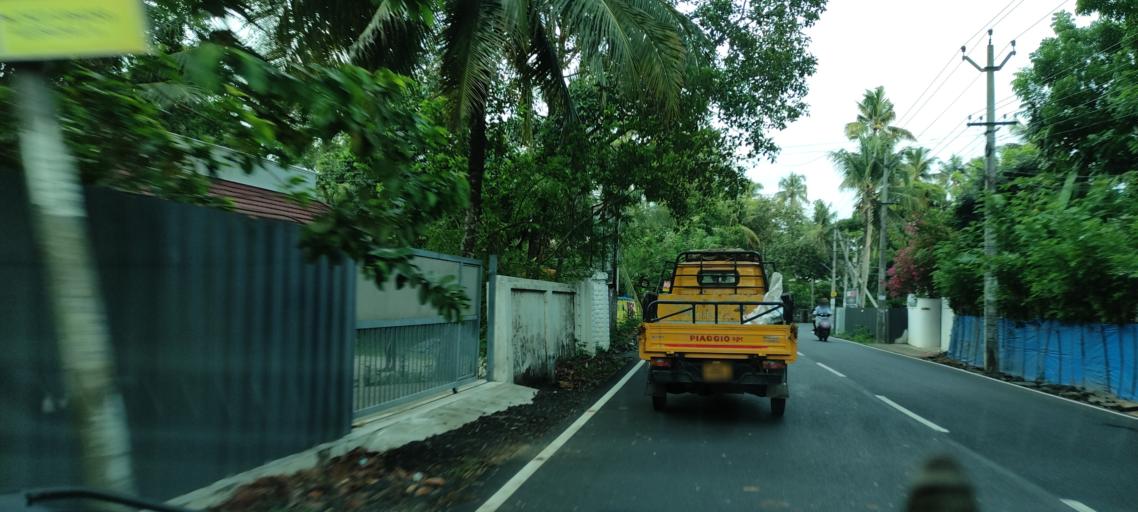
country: IN
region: Kerala
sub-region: Alappuzha
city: Kutiatodu
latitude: 9.8281
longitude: 76.3421
